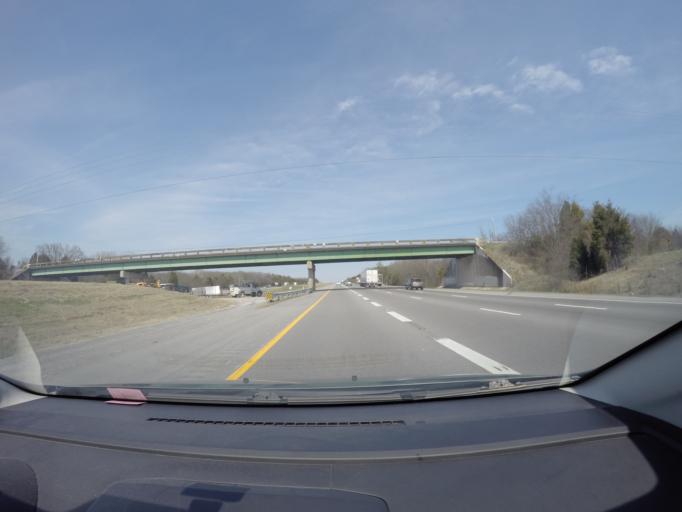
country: US
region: Tennessee
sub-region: Rutherford County
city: Smyrna
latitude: 35.9524
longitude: -86.5512
